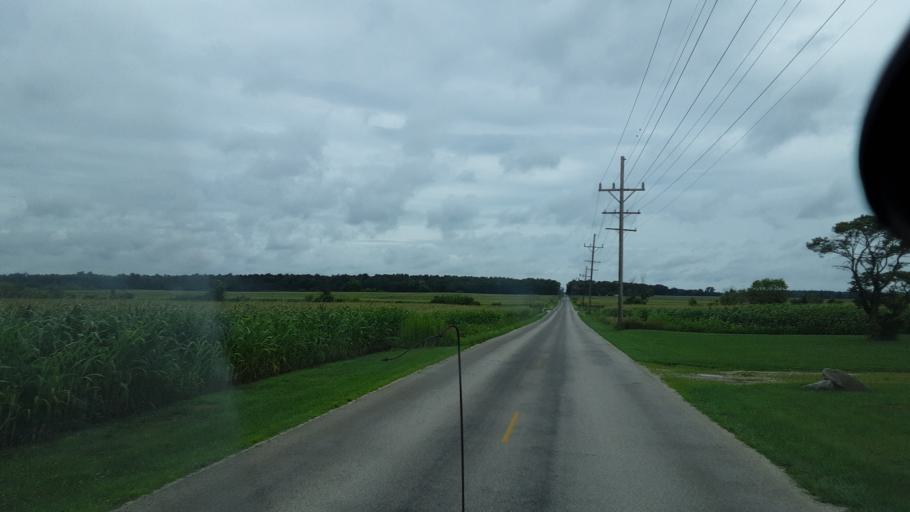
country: US
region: Indiana
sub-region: Jay County
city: Portland
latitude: 40.4491
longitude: -85.0199
